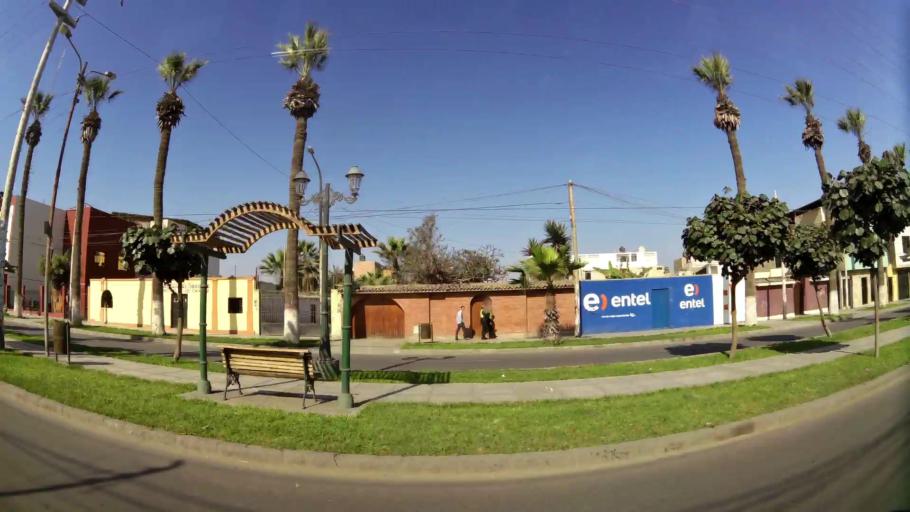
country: PE
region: Ica
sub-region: Provincia de Chincha
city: Chincha Alta
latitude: -13.4144
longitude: -76.1324
